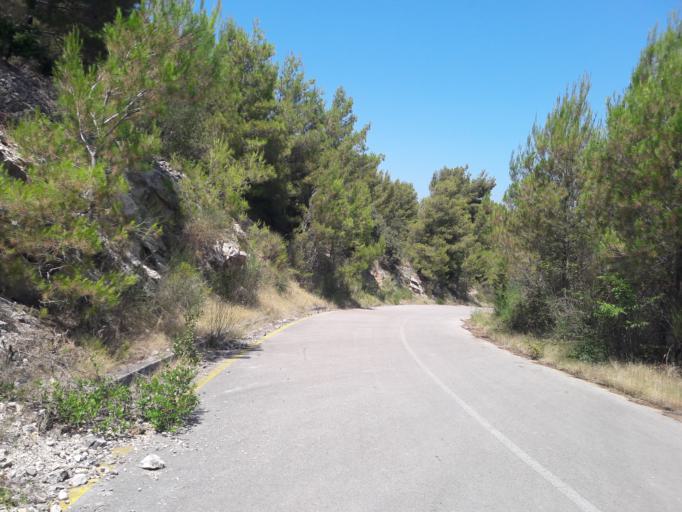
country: HR
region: Sibensko-Kniniska
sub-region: Grad Sibenik
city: Sibenik
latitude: 43.7012
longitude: 15.8456
